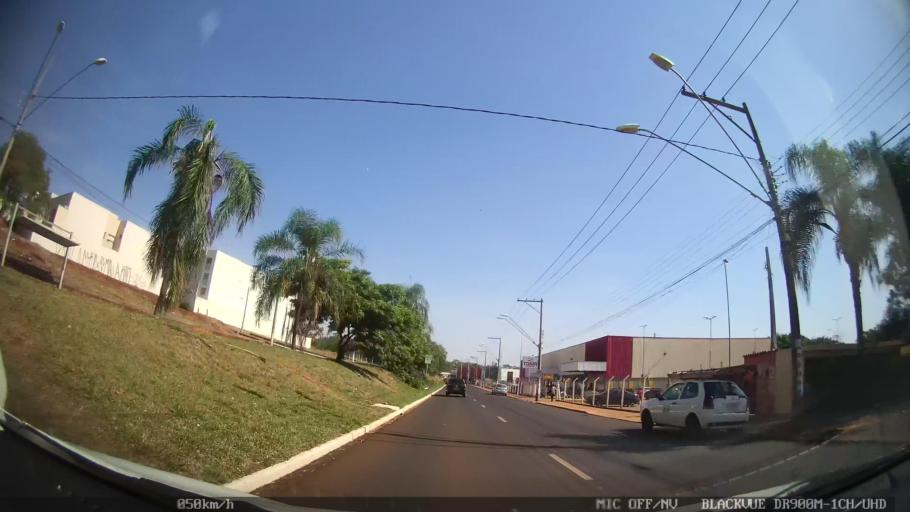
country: BR
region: Sao Paulo
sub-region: Ribeirao Preto
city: Ribeirao Preto
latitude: -21.2025
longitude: -47.8249
